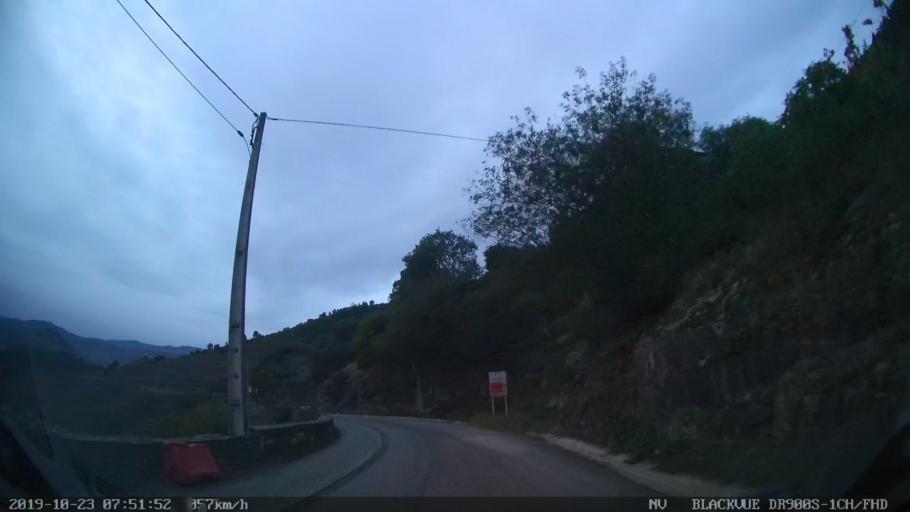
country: PT
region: Vila Real
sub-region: Sabrosa
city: Vilela
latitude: 41.2131
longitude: -7.5525
